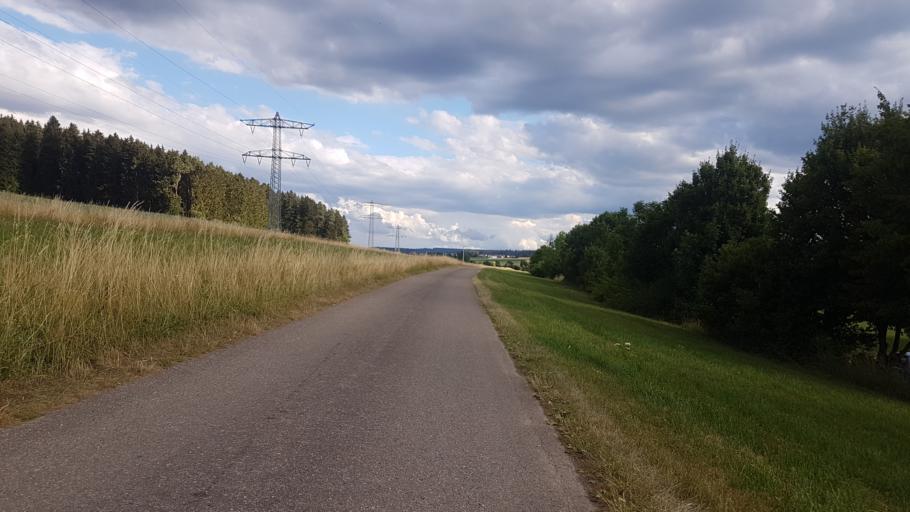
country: DE
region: Baden-Wuerttemberg
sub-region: Freiburg Region
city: Braunlingen
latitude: 47.9970
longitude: 8.4188
